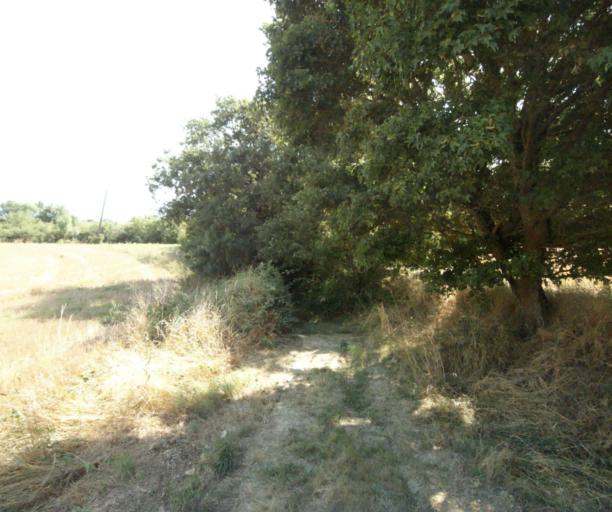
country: FR
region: Midi-Pyrenees
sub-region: Departement de la Haute-Garonne
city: Saint-Felix-Lauragais
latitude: 43.4490
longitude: 1.8697
